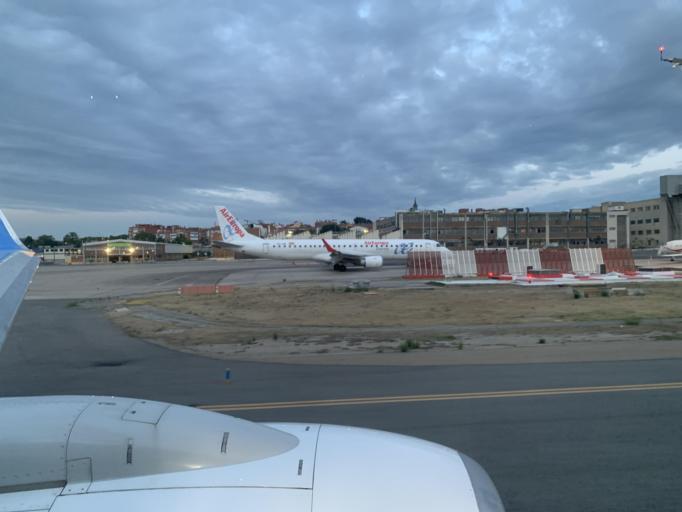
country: ES
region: Madrid
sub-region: Provincia de Madrid
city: Barajas de Madrid
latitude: 40.4765
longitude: -3.5715
